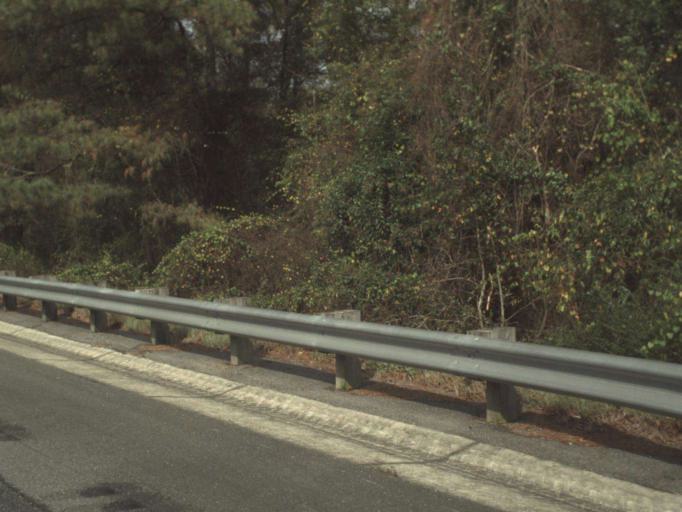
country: US
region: Florida
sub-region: Gadsden County
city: Quincy
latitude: 30.5325
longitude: -84.5749
